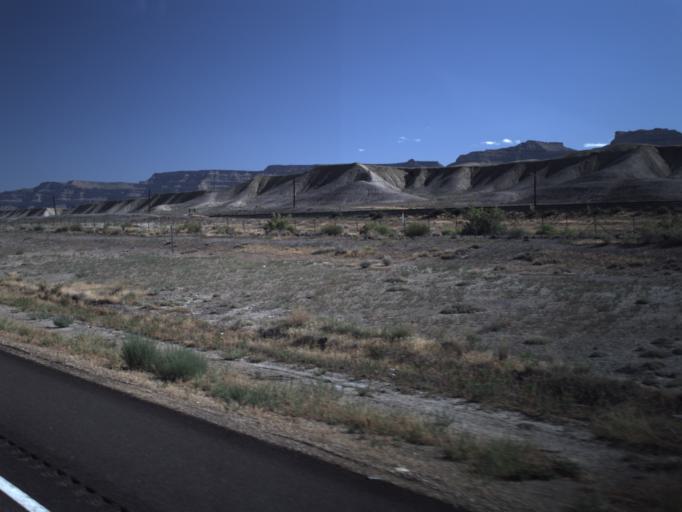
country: US
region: Utah
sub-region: Carbon County
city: East Carbon City
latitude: 39.0407
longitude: -110.3076
